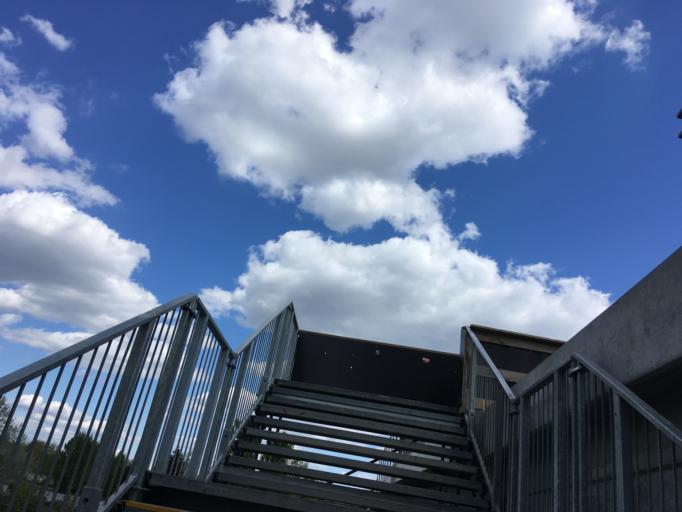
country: DE
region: Berlin
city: Biesdorf
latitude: 52.5127
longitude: 13.5498
